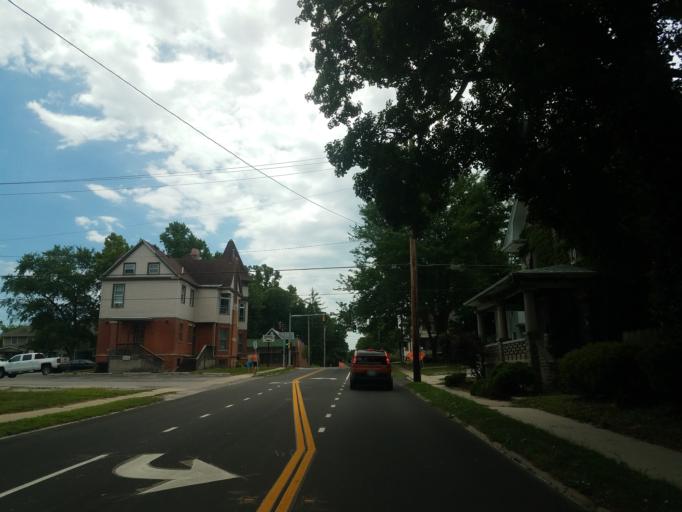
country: US
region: Illinois
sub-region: McLean County
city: Bloomington
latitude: 40.4786
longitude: -88.9846
